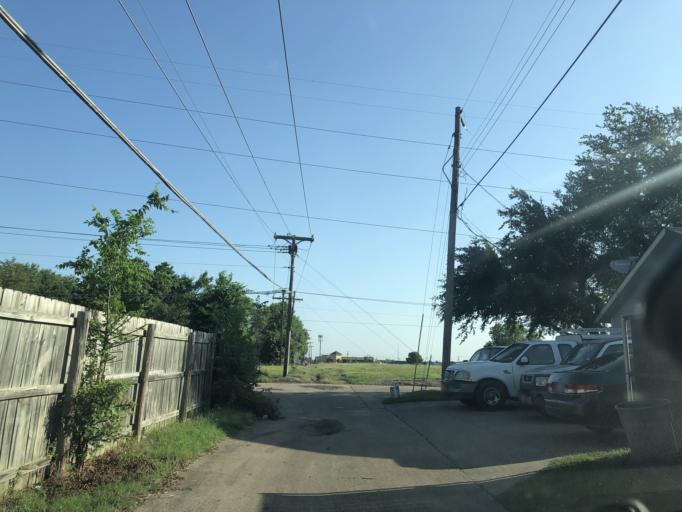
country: US
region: Texas
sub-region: Dallas County
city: Sunnyvale
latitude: 32.8197
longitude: -96.5972
